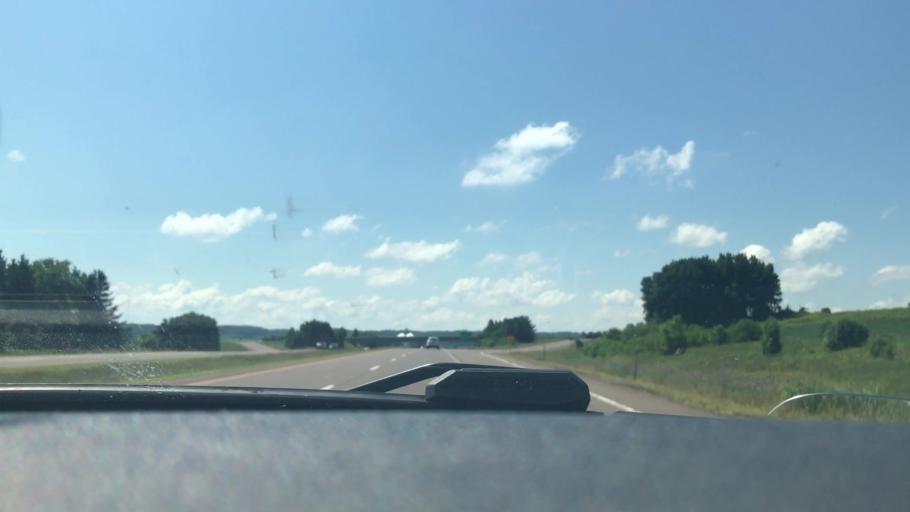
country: US
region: Wisconsin
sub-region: Chippewa County
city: Chippewa Falls
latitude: 45.0040
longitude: -91.4423
